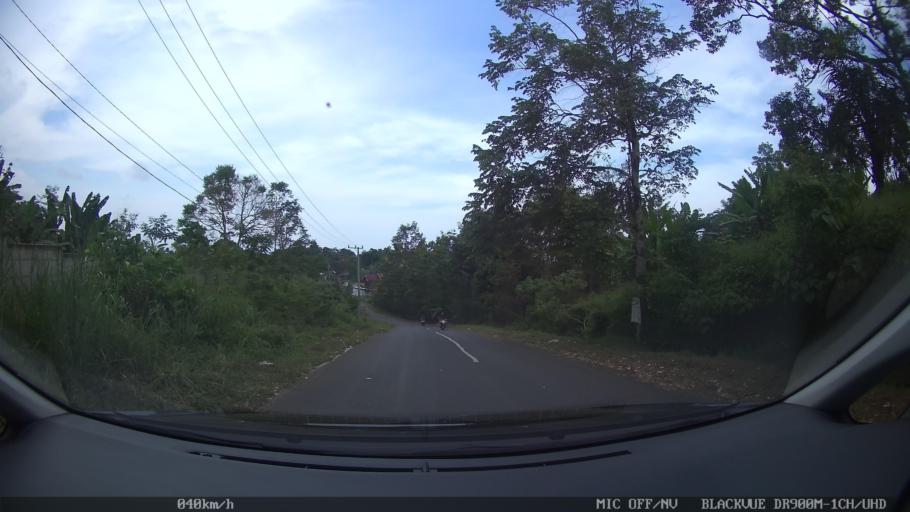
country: ID
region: Lampung
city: Bandarlampung
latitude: -5.4294
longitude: 105.2018
